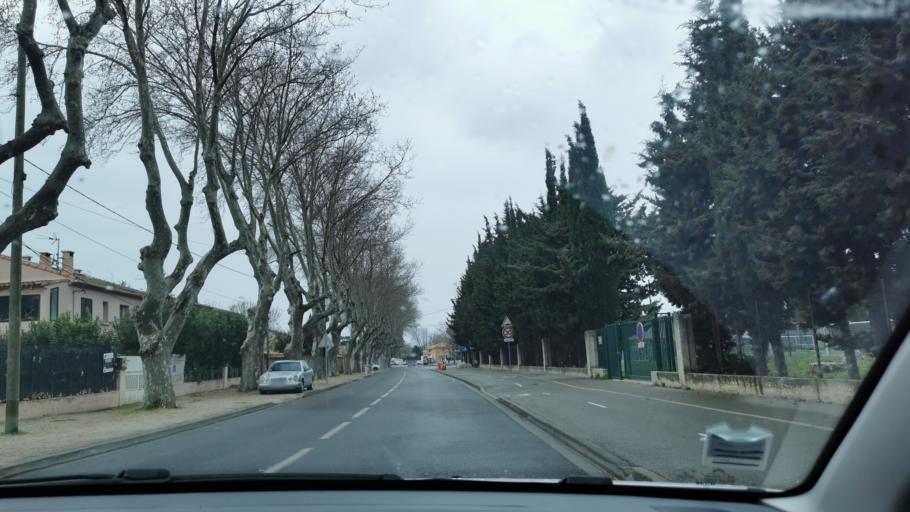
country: FR
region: Provence-Alpes-Cote d'Azur
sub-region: Departement des Bouches-du-Rhone
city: Pelissanne
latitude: 43.6305
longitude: 5.1584
